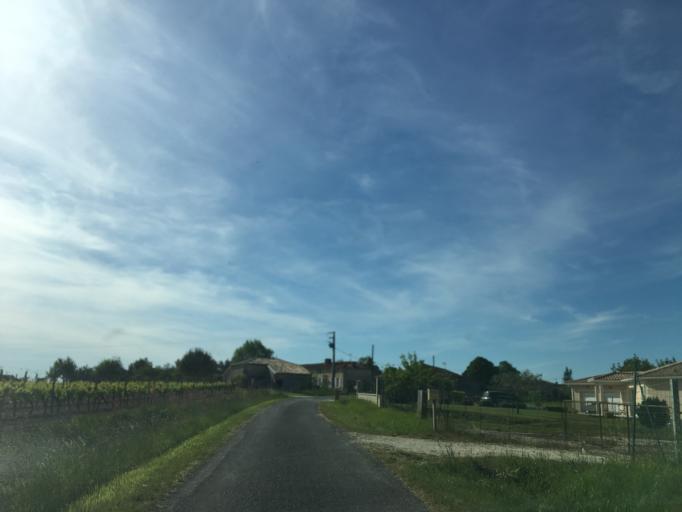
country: FR
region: Poitou-Charentes
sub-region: Departement de la Charente-Maritime
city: Mirambeau
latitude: 45.3410
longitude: -0.5840
